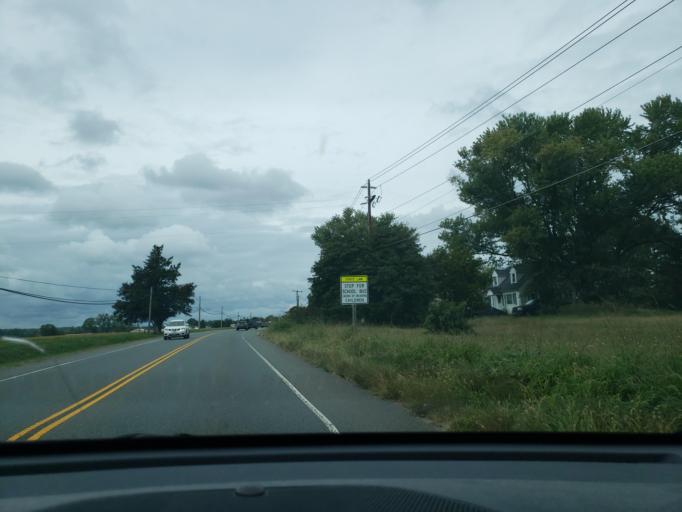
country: US
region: Virginia
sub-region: City of Fredericksburg
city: Fredericksburg
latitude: 38.2646
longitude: -77.4394
